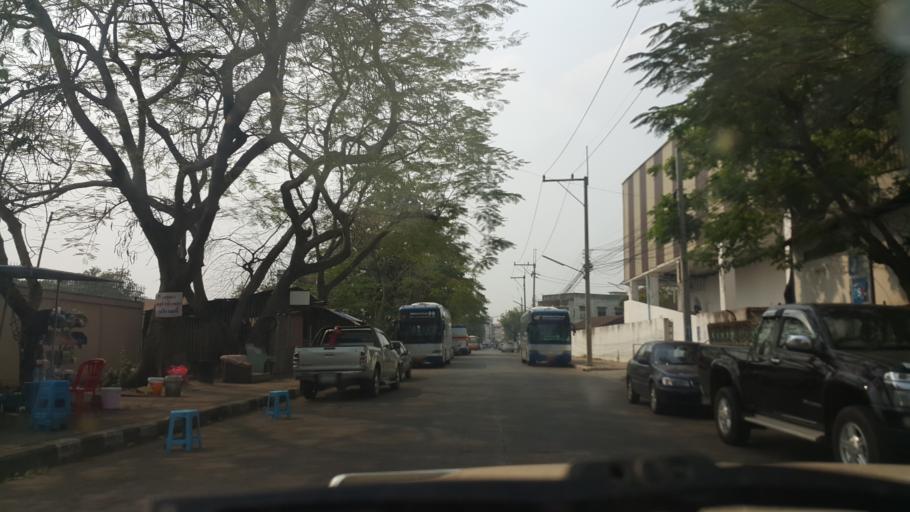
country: TH
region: Changwat Udon Thani
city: Udon Thani
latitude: 17.4015
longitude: 102.8039
